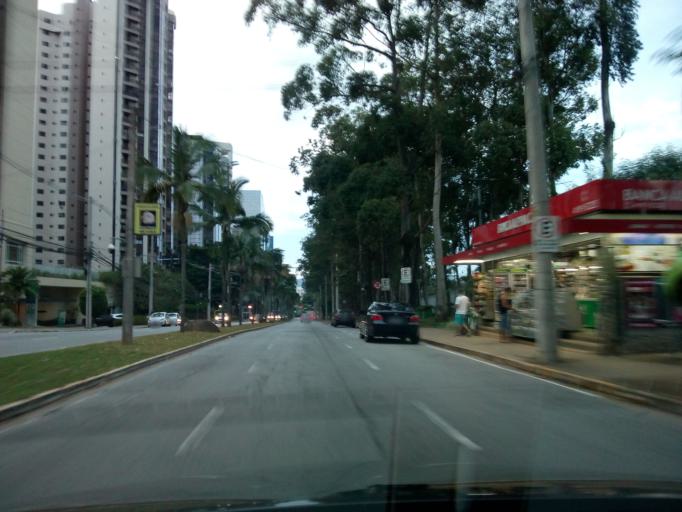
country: BR
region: Sao Paulo
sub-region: Carapicuiba
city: Carapicuiba
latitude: -23.4920
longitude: -46.8456
